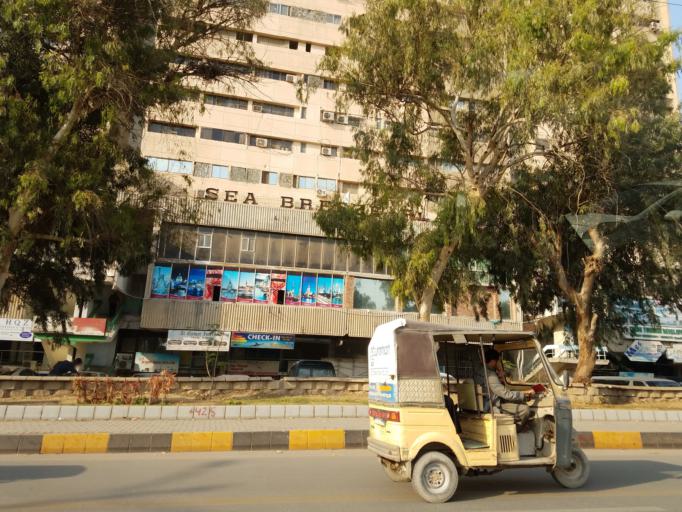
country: PK
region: Sindh
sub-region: Karachi District
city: Karachi
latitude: 24.8572
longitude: 67.0440
